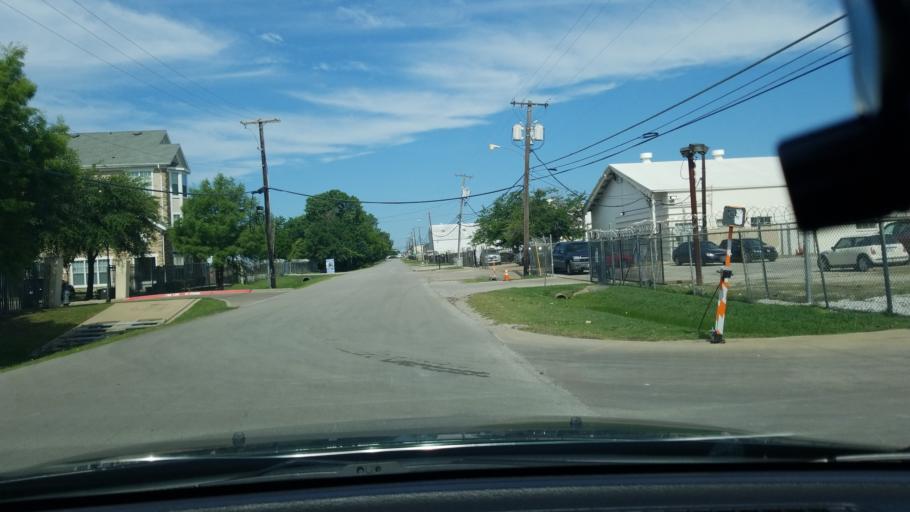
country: US
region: Texas
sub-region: Dallas County
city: Balch Springs
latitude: 32.7743
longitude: -96.6772
